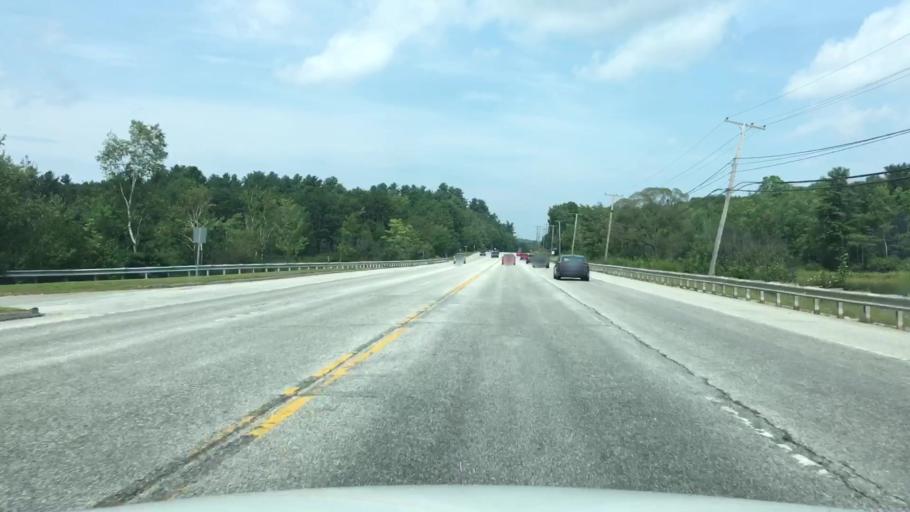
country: US
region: Maine
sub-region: Androscoggin County
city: Lewiston
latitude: 44.1454
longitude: -70.2282
